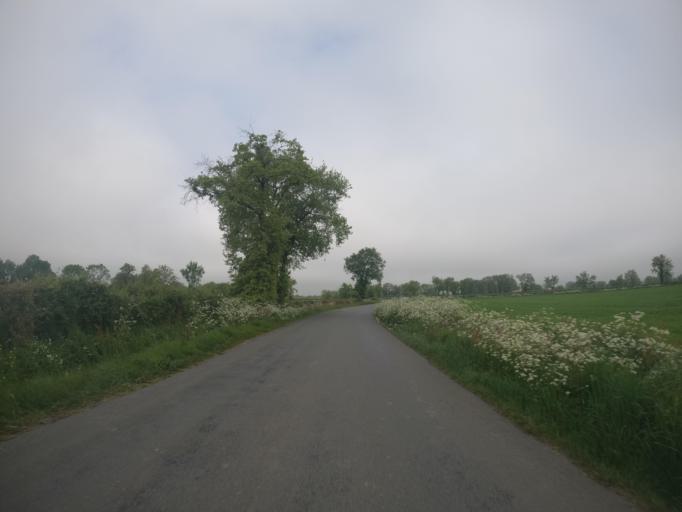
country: FR
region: Poitou-Charentes
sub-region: Departement des Deux-Sevres
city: Saint-Varent
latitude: 46.8751
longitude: -0.3179
